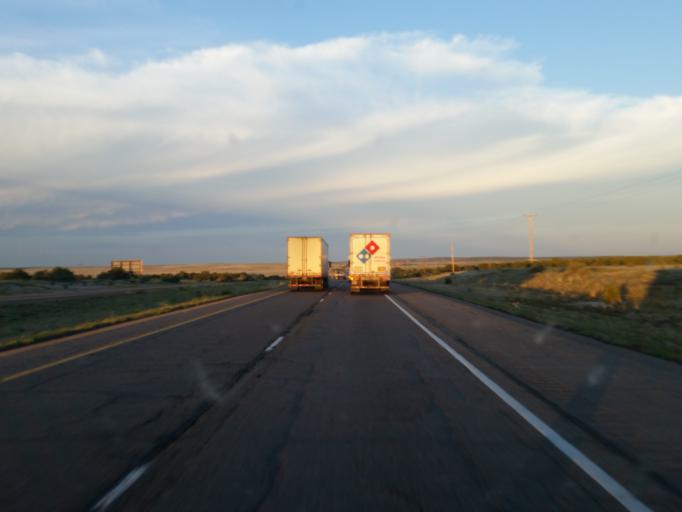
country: US
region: New Mexico
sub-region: San Miguel County
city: Las Vegas
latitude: 34.9929
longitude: -105.3261
